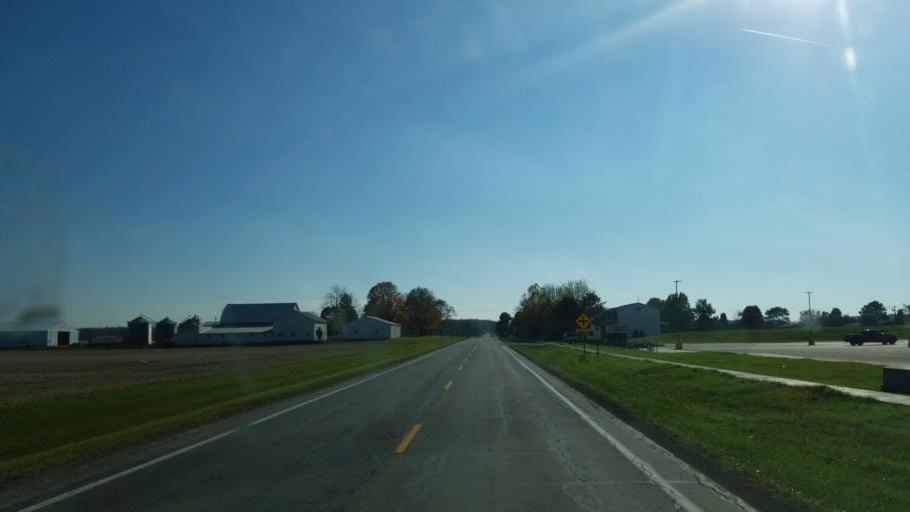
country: US
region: Ohio
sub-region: Lorain County
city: Wellington
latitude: 41.1506
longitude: -82.2180
